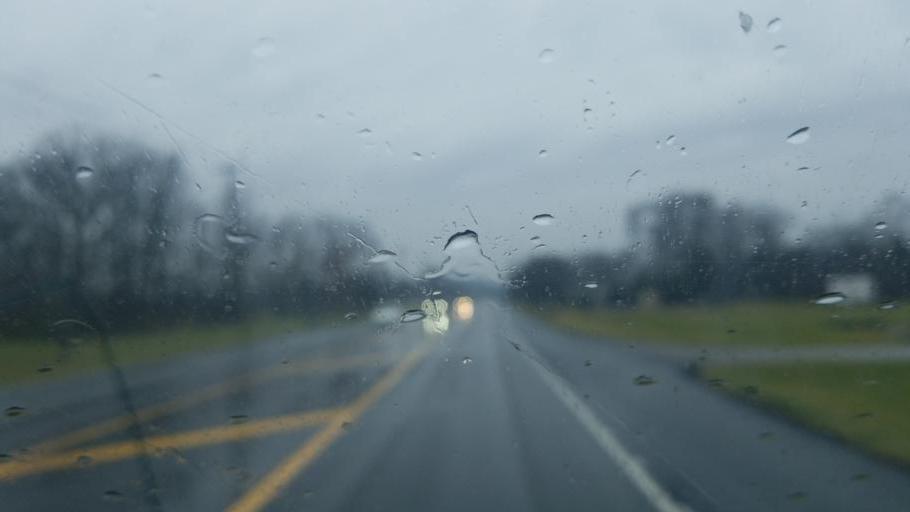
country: US
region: Indiana
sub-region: Bartholomew County
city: Lowell
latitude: 39.1970
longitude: -85.9997
